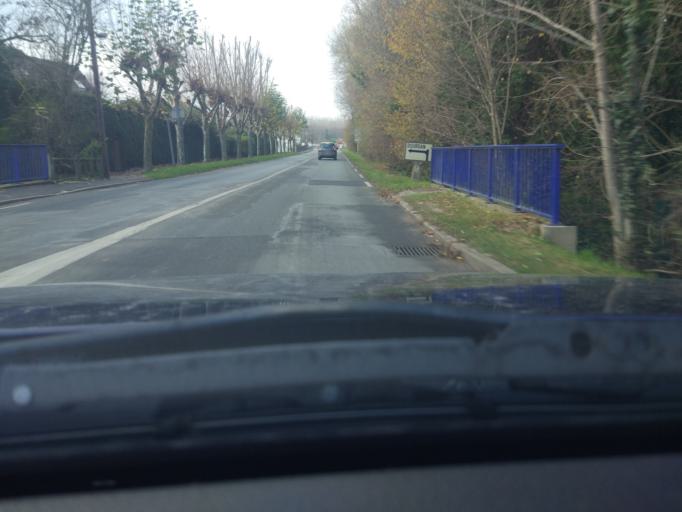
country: FR
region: Ile-de-France
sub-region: Departement de l'Essonne
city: Bruyeres-le-Chatel
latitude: 48.5771
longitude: 2.1957
